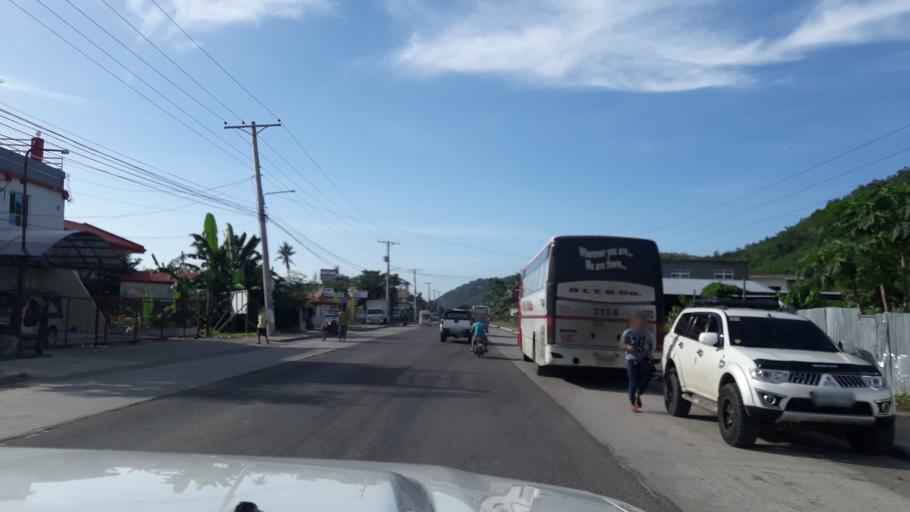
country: PH
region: Eastern Visayas
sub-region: Province of Leyte
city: Pawing
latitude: 11.2046
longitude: 124.9914
